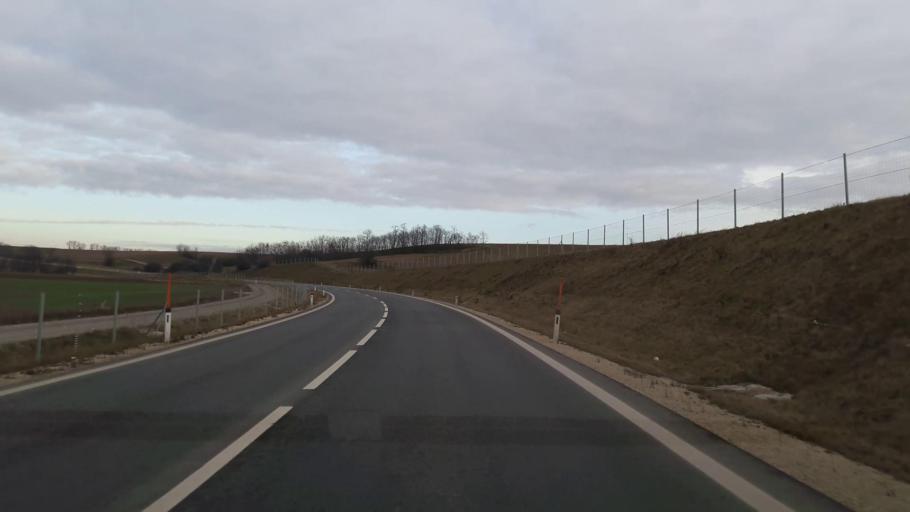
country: AT
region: Lower Austria
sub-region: Politischer Bezirk Mistelbach
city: Mistelbach
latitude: 48.5729
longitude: 16.5558
